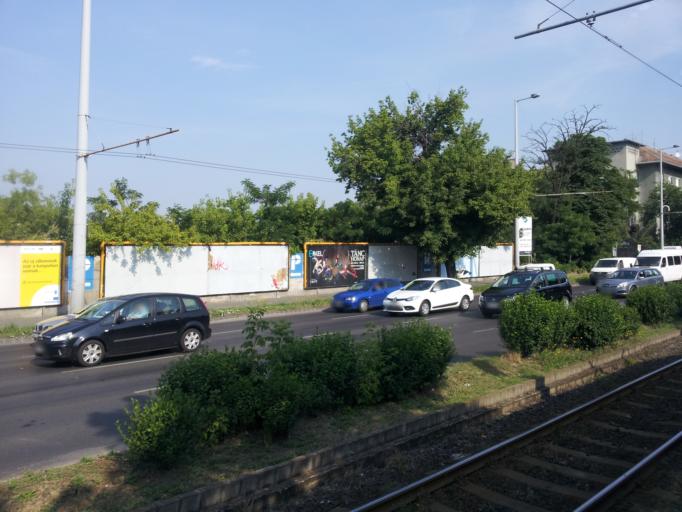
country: HU
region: Budapest
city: Budapest XIV. keruelet
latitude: 47.4973
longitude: 19.1090
